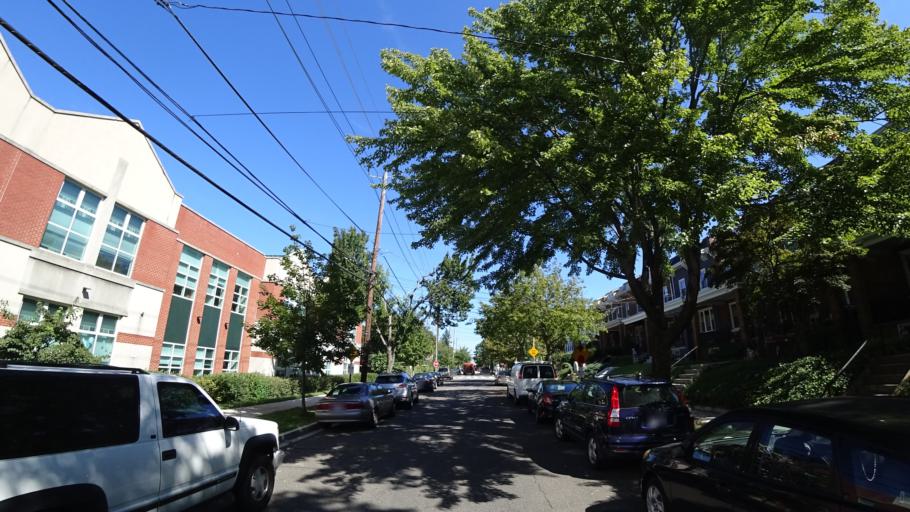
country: US
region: Maryland
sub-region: Prince George's County
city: Chillum
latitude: 38.9479
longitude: -77.0174
